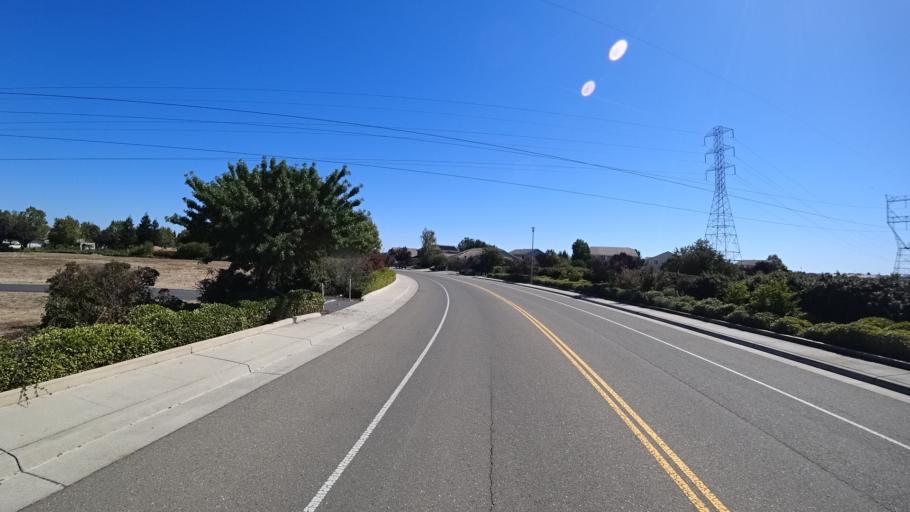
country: US
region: California
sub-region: Sacramento County
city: Elk Grove
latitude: 38.4024
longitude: -121.3503
